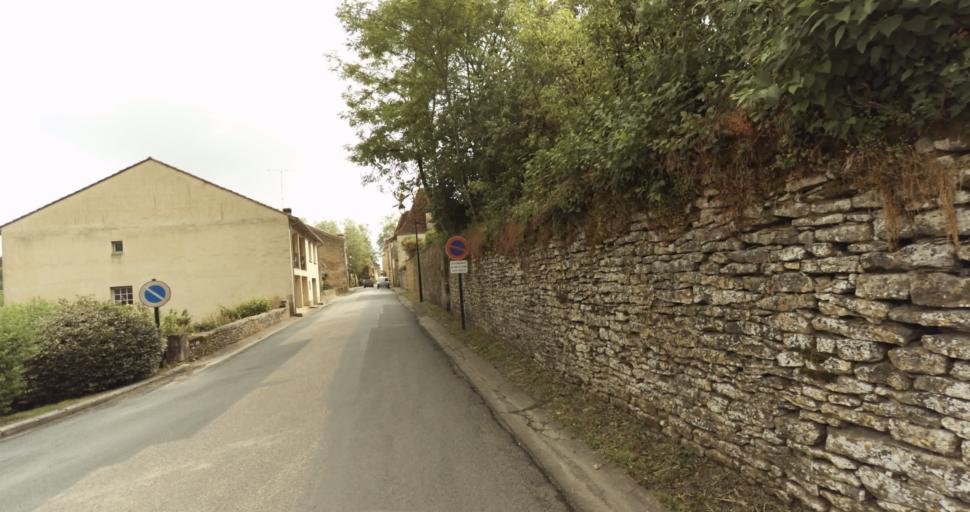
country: FR
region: Aquitaine
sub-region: Departement de la Dordogne
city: Vergt
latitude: 44.9453
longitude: 0.8073
